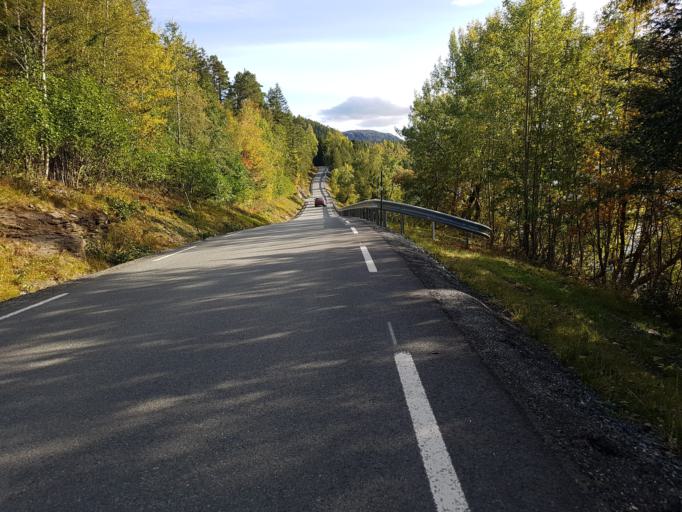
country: NO
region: Sor-Trondelag
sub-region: Malvik
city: Malvik
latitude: 63.3598
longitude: 10.6319
